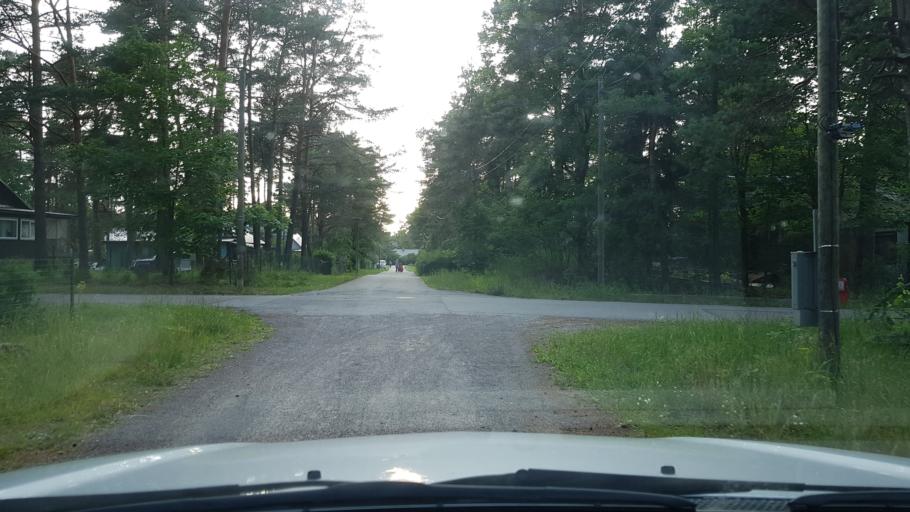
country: EE
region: Ida-Virumaa
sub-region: Narva-Joesuu linn
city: Narva-Joesuu
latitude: 59.4549
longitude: 28.0530
